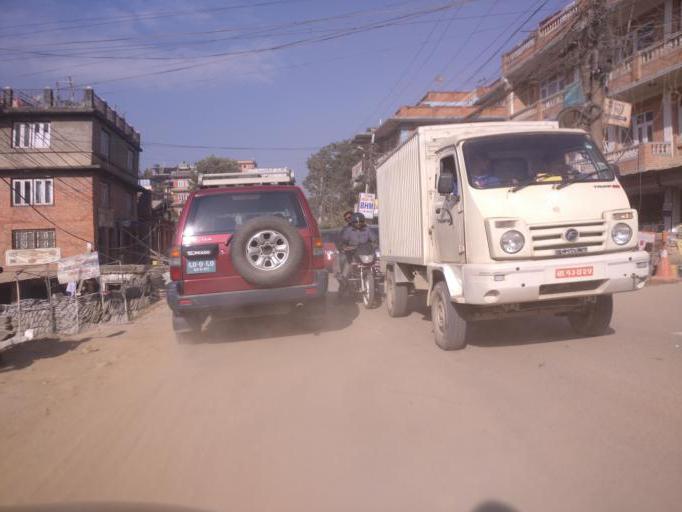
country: NP
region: Central Region
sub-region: Bagmati Zone
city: Patan
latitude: 27.6691
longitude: 85.3064
